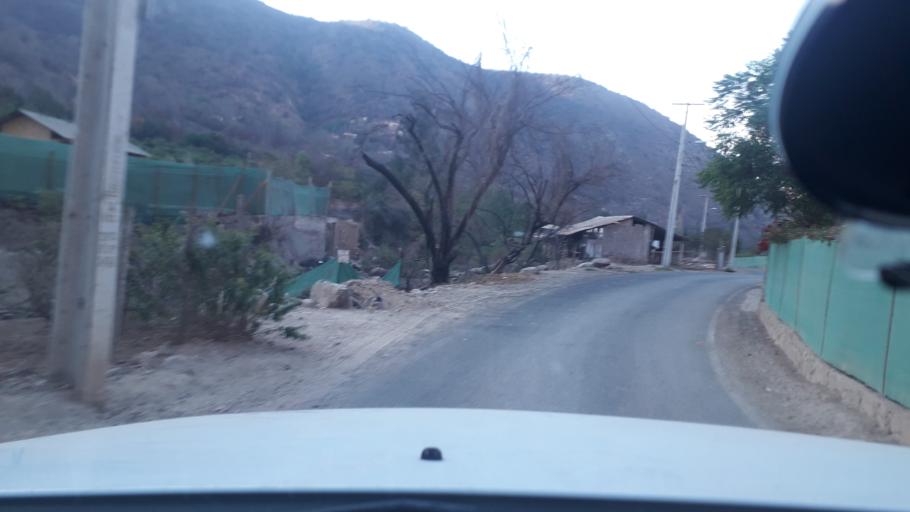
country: CL
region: Valparaiso
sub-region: Provincia de Marga Marga
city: Limache
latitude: -33.0643
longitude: -71.1175
